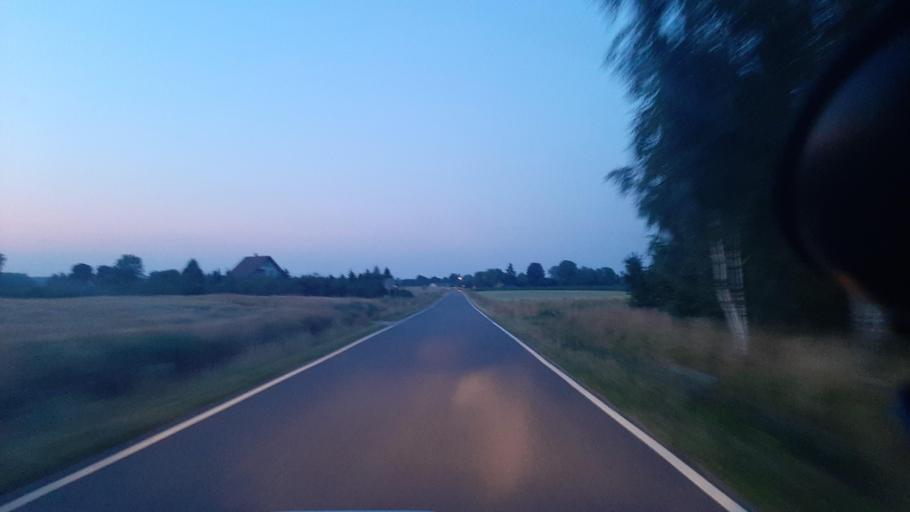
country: PL
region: Lublin Voivodeship
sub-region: Powiat lubelski
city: Garbow
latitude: 51.3933
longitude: 22.3135
